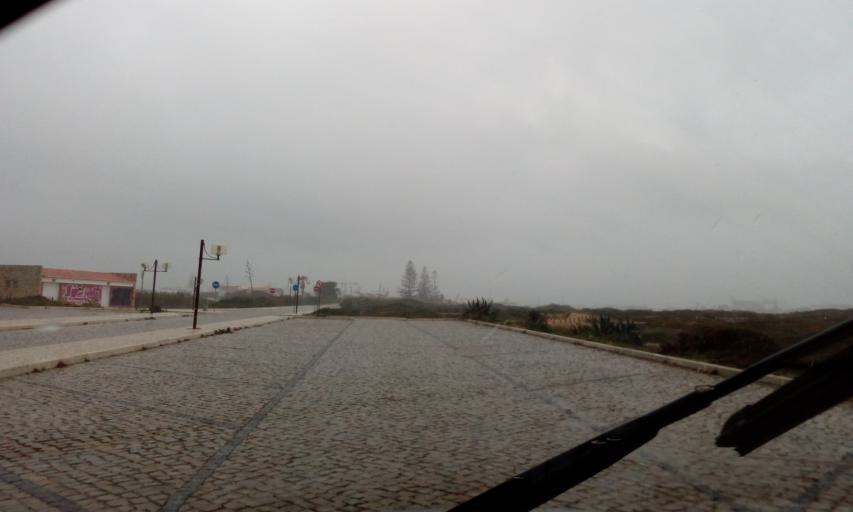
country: PT
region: Faro
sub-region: Vila do Bispo
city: Sagres
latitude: 37.0037
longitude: -8.9451
